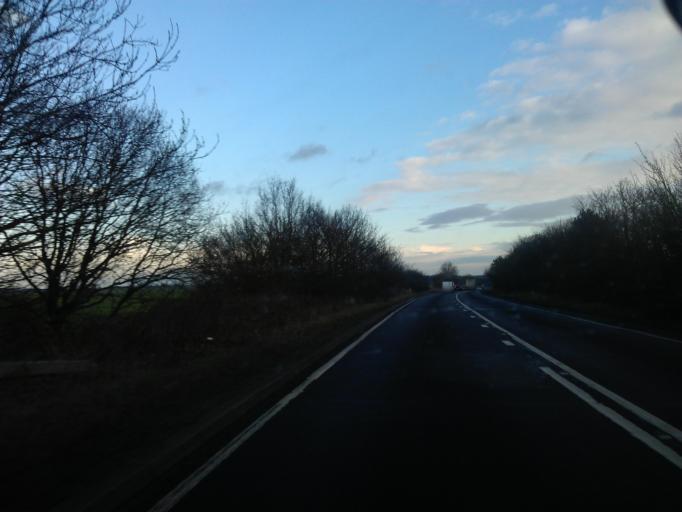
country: GB
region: England
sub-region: Essex
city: Mistley
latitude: 51.9139
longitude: 1.1436
